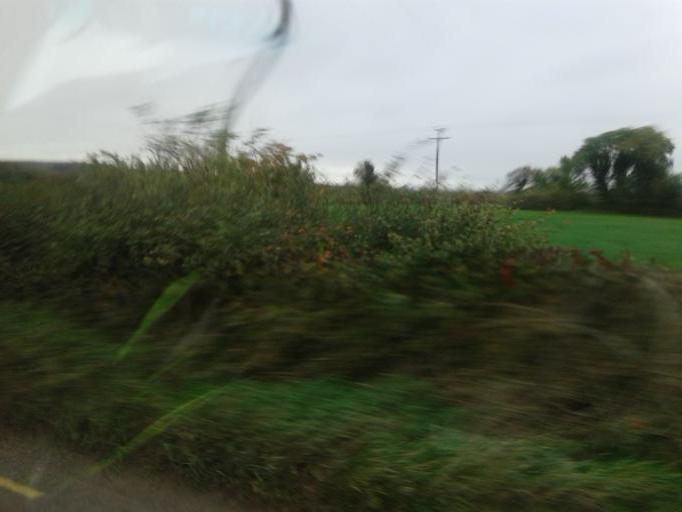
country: IE
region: Leinster
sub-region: Uibh Fhaili
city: Birr
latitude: 52.9590
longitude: -8.0182
